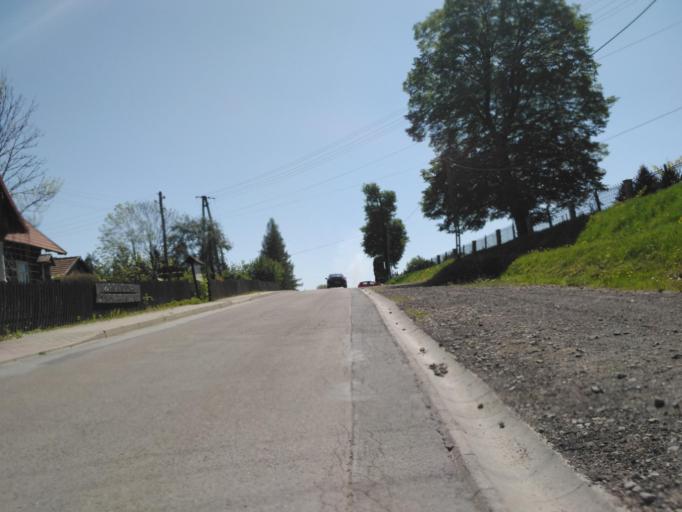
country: PL
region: Subcarpathian Voivodeship
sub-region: Powiat krosnienski
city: Miejsce Piastowe
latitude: 49.6120
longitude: 21.7578
